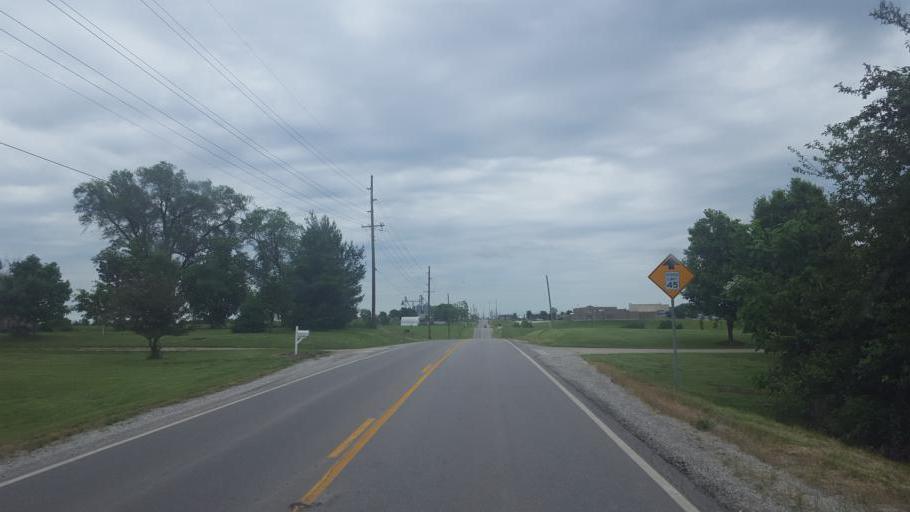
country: US
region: Missouri
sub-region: Moniteau County
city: California
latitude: 38.6358
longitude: -92.6001
